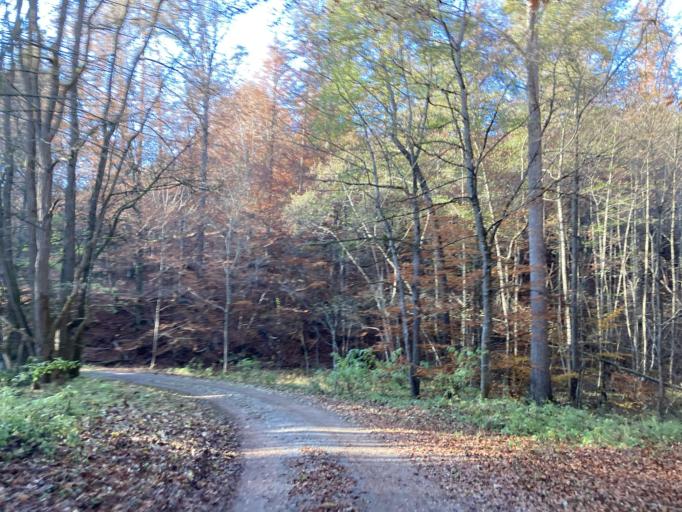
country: DE
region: Baden-Wuerttemberg
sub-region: Tuebingen Region
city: Tuebingen
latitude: 48.5482
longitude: 8.9959
